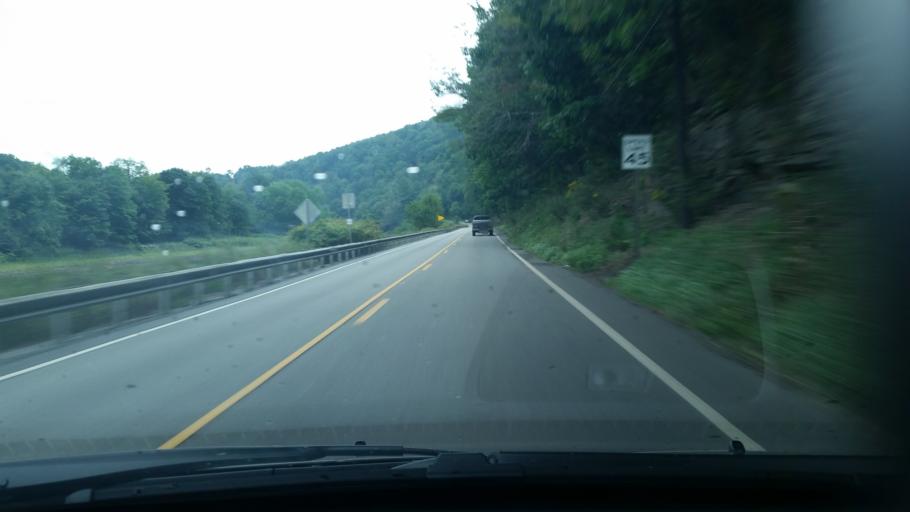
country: US
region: Pennsylvania
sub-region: Clearfield County
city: Clearfield
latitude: 41.0635
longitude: -78.3734
